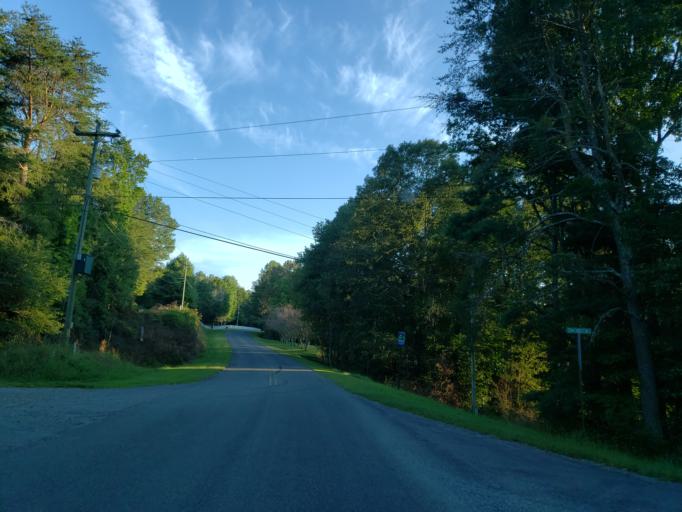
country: US
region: Georgia
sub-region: Gilmer County
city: Ellijay
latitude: 34.6614
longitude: -84.3369
